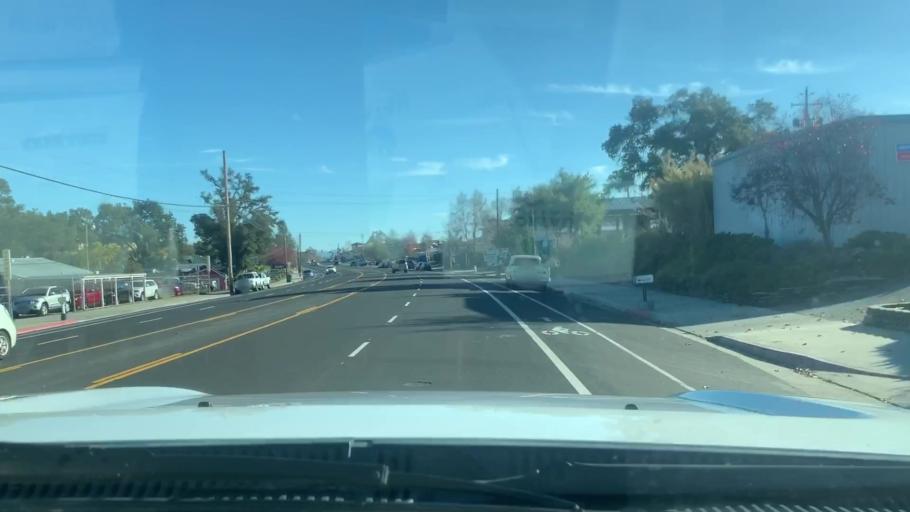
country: US
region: California
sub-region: San Luis Obispo County
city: Atascadero
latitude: 35.4700
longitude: -120.6526
